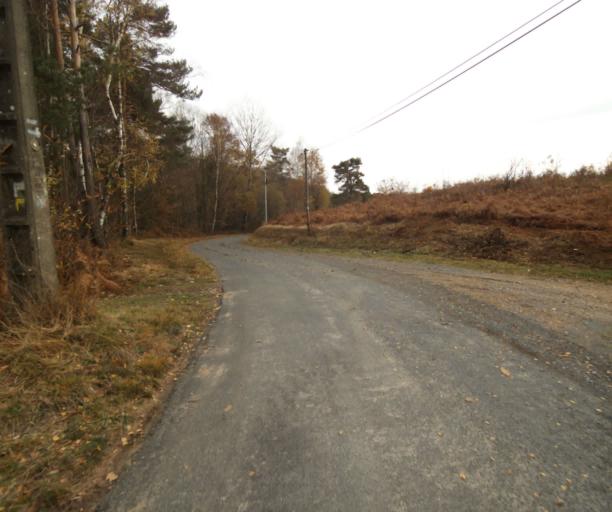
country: FR
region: Limousin
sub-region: Departement de la Correze
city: Sainte-Fortunade
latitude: 45.1885
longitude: 1.7557
